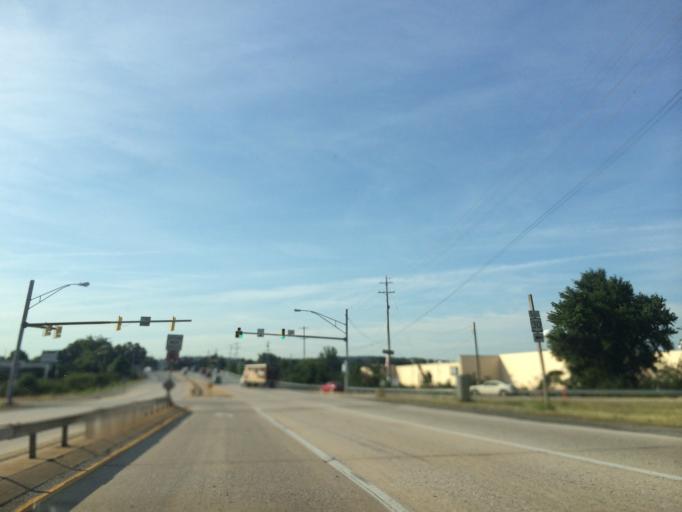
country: US
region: Pennsylvania
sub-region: York County
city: Yorklyn
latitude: 39.9863
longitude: -76.6675
